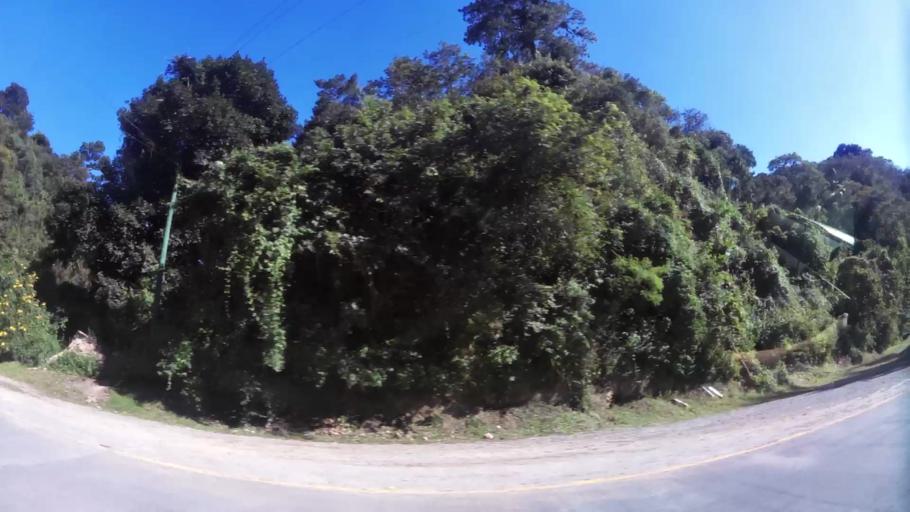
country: GT
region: Sacatepequez
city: Santa Lucia Milpas Altas
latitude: 14.5698
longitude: -90.6911
